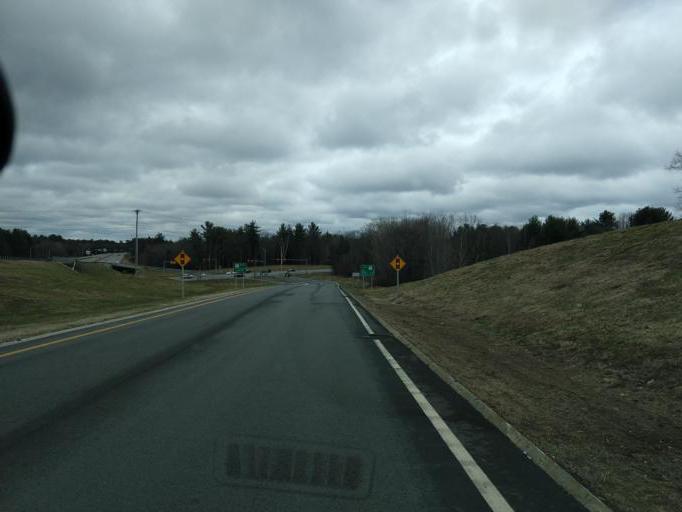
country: US
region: New Hampshire
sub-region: Strafford County
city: Rochester
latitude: 43.2828
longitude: -70.9817
